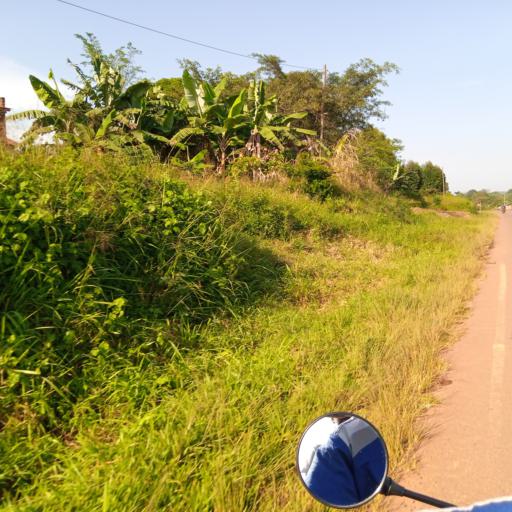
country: UG
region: Central Region
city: Masaka
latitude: -0.4294
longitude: 31.6658
